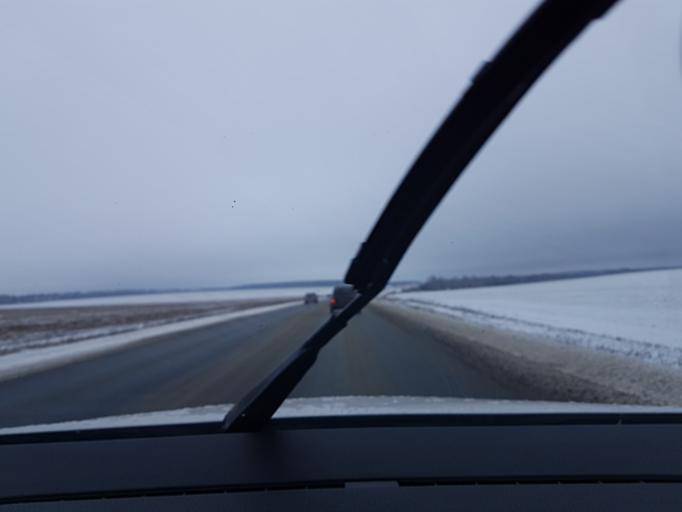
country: RU
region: Moskovskaya
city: Uzunovo
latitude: 54.6029
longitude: 38.4090
